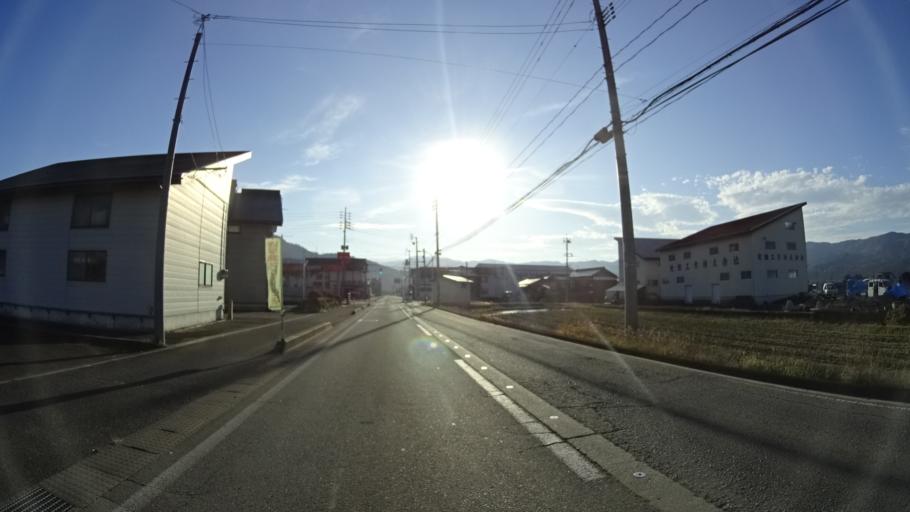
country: JP
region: Niigata
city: Shiozawa
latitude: 37.0170
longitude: 138.8584
